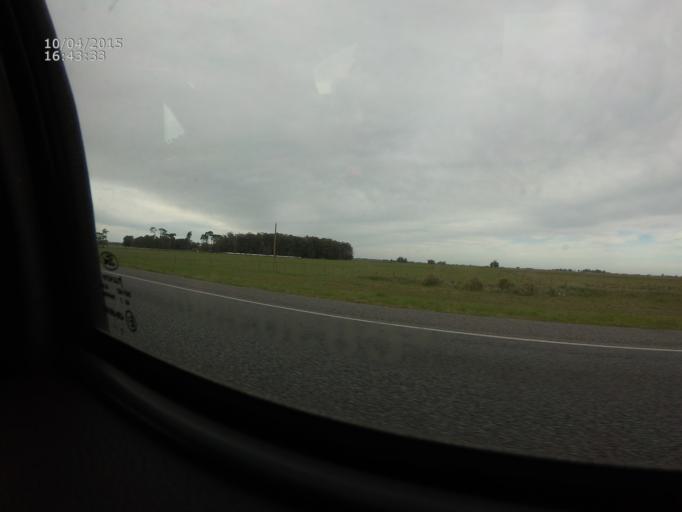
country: AR
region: Buenos Aires
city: Mar del Plata
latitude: -37.7413
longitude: -57.6462
